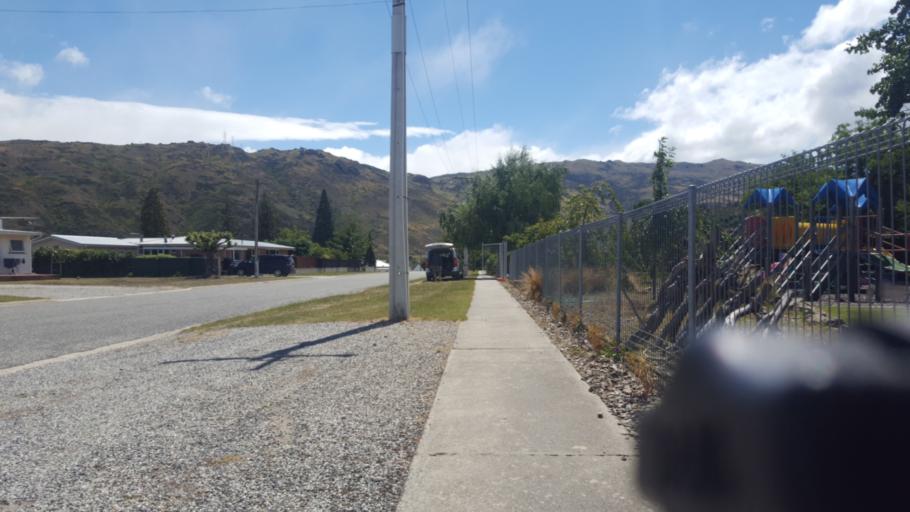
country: NZ
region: Otago
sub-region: Queenstown-Lakes District
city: Wanaka
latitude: -45.1890
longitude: 169.3225
